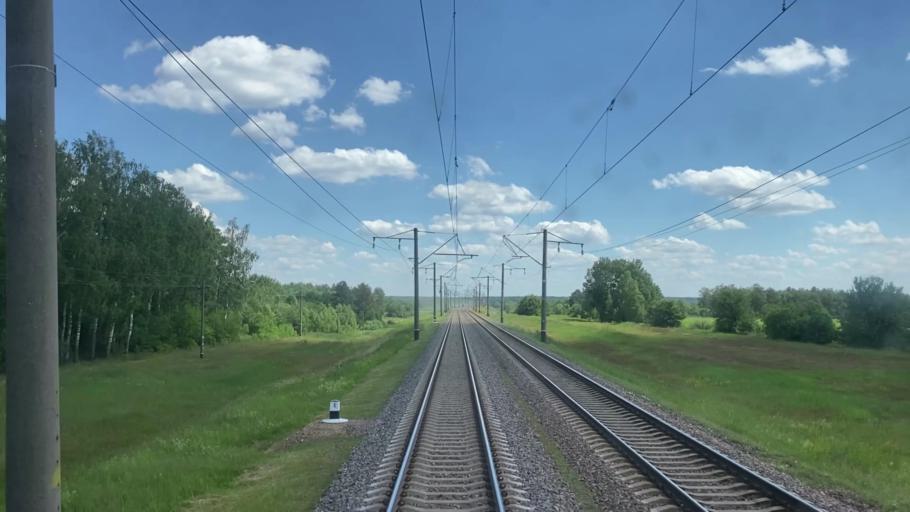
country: BY
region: Brest
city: Ivatsevichy
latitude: 52.8389
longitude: 25.5279
